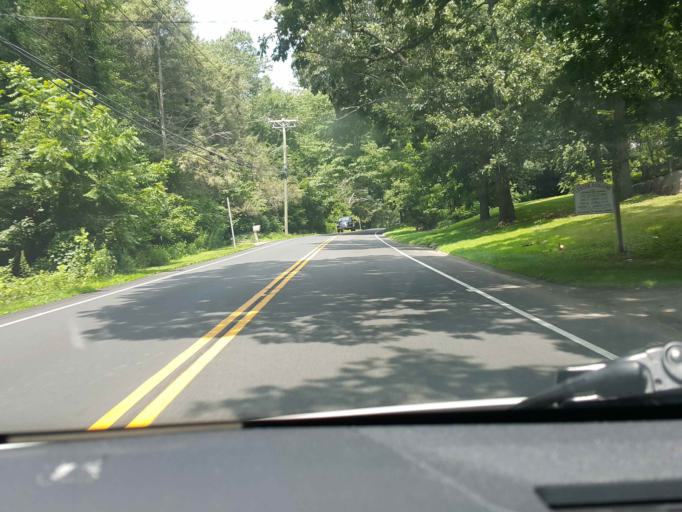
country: US
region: Connecticut
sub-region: New Haven County
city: Guilford
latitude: 41.3031
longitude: -72.6882
